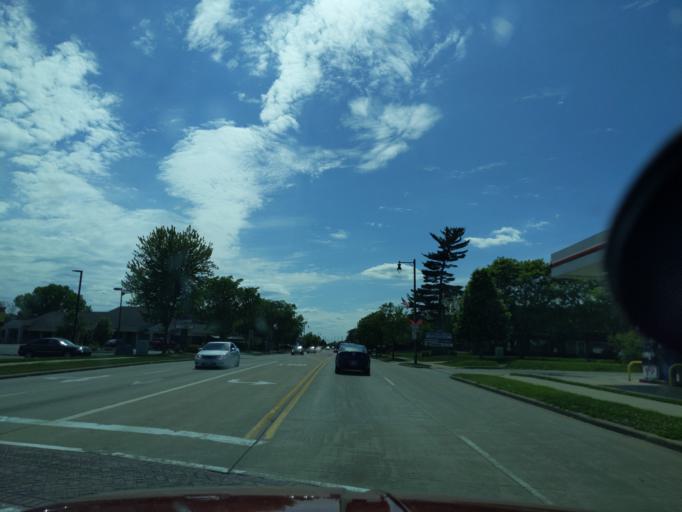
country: US
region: Wisconsin
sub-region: Dane County
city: Sun Prairie
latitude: 43.1791
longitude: -89.2368
